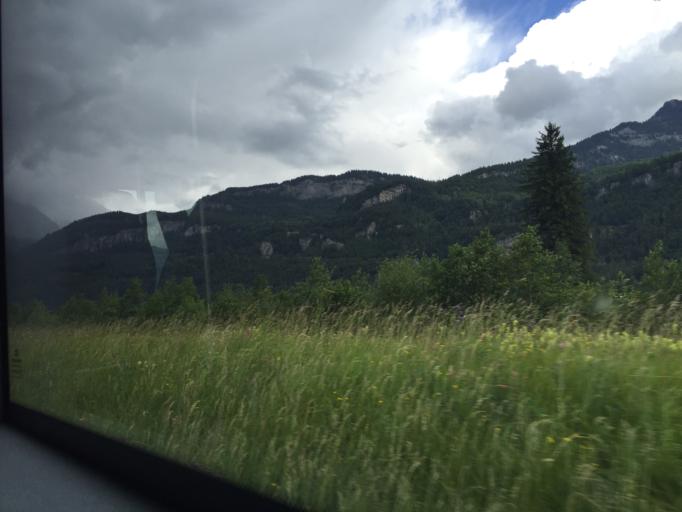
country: CH
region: Bern
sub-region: Interlaken-Oberhasli District
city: Meiringen
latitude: 46.7302
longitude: 8.1654
